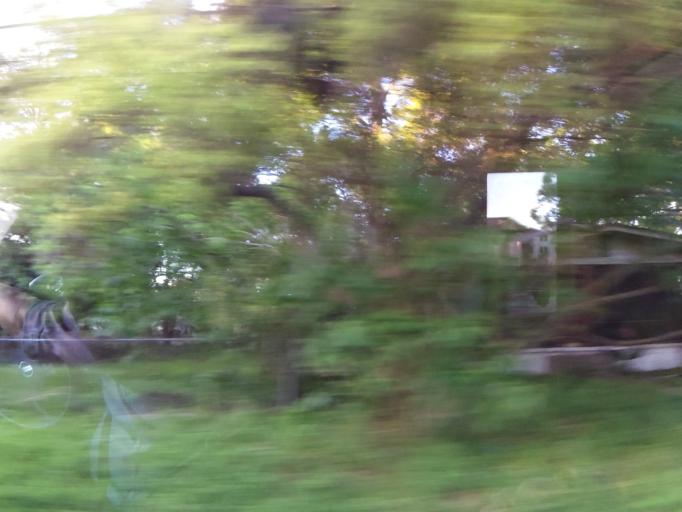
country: US
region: Florida
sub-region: Duval County
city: Jacksonville
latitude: 30.3330
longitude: -81.7090
